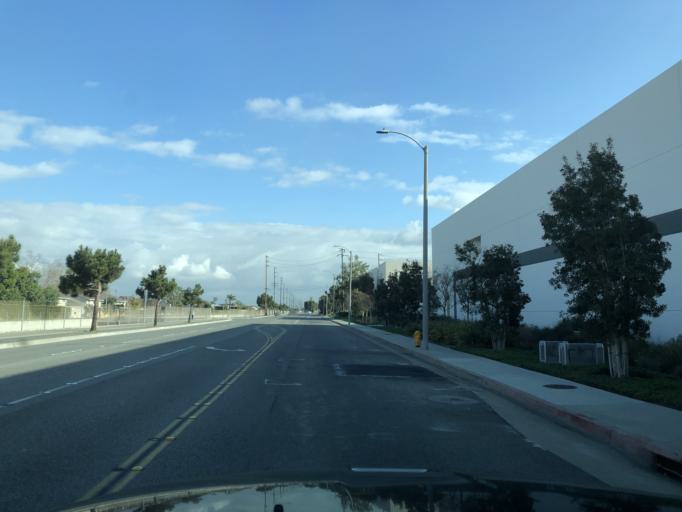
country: US
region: California
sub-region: Orange County
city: Westminster
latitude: 33.7524
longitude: -118.0387
